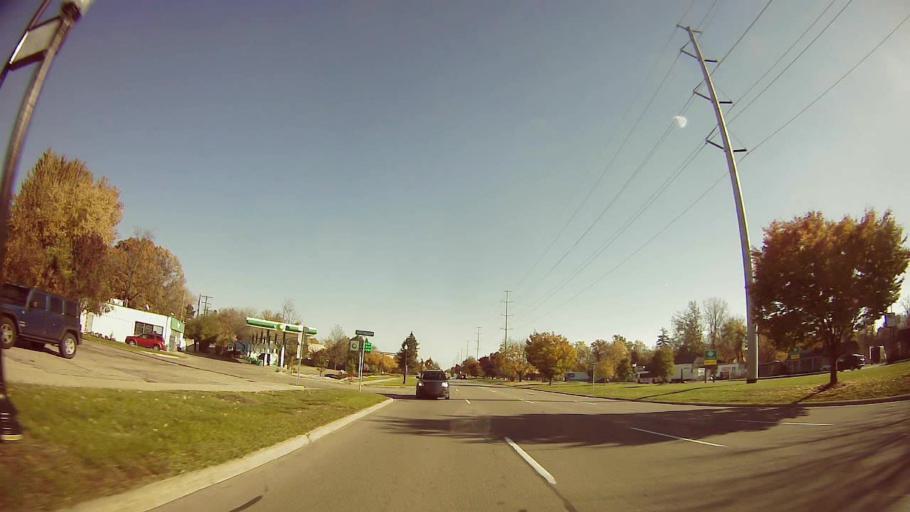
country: US
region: Michigan
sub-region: Oakland County
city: Farmington
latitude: 42.4466
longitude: -83.3321
